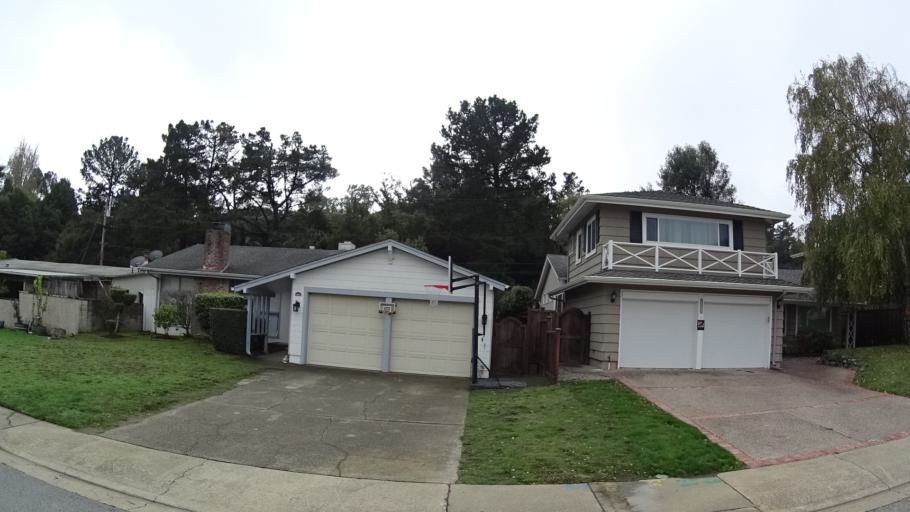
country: US
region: California
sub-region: San Mateo County
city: San Bruno
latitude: 37.6044
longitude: -122.4218
